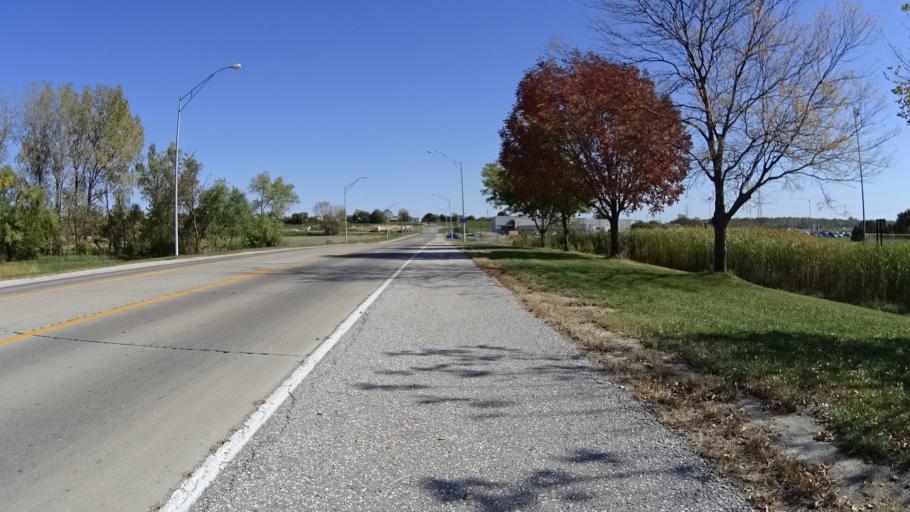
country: US
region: Nebraska
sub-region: Sarpy County
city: Papillion
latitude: 41.1564
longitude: -96.0272
